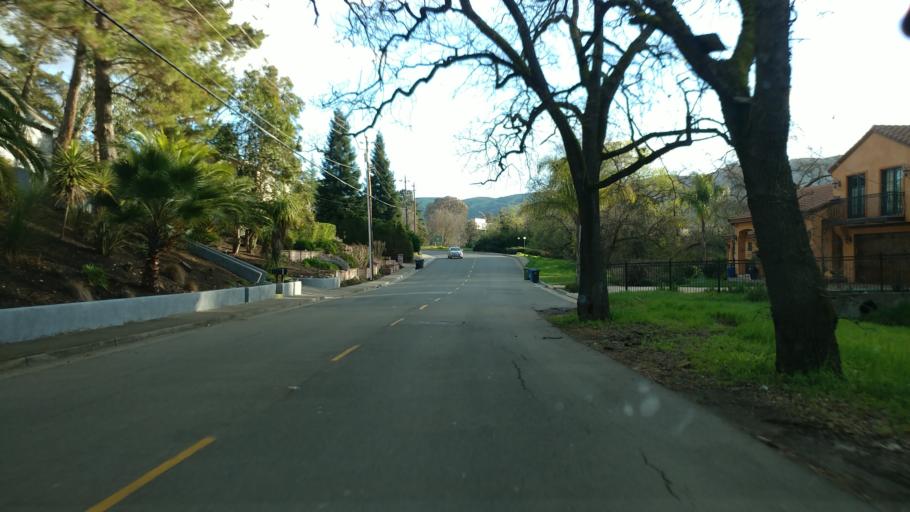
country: US
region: California
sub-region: Contra Costa County
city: Danville
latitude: 37.8320
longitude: -121.9996
